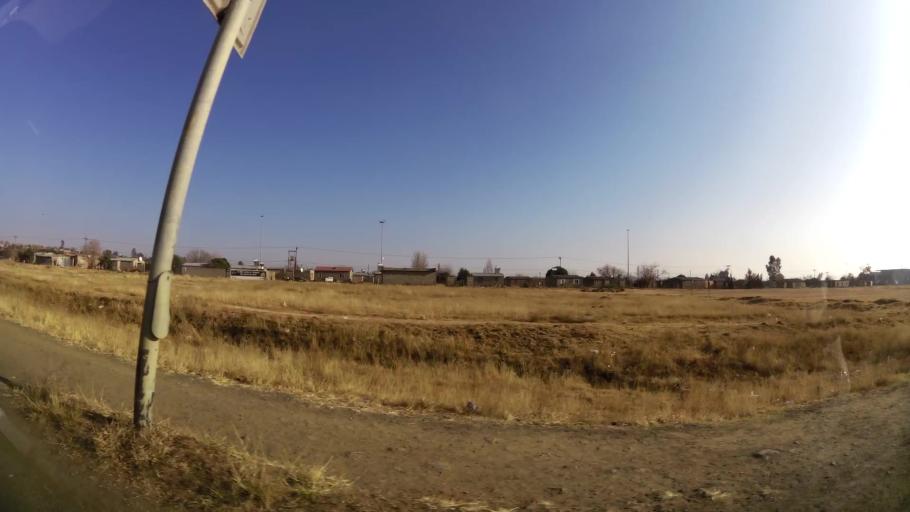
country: ZA
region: Orange Free State
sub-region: Mangaung Metropolitan Municipality
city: Bloemfontein
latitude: -29.1626
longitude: 26.2548
